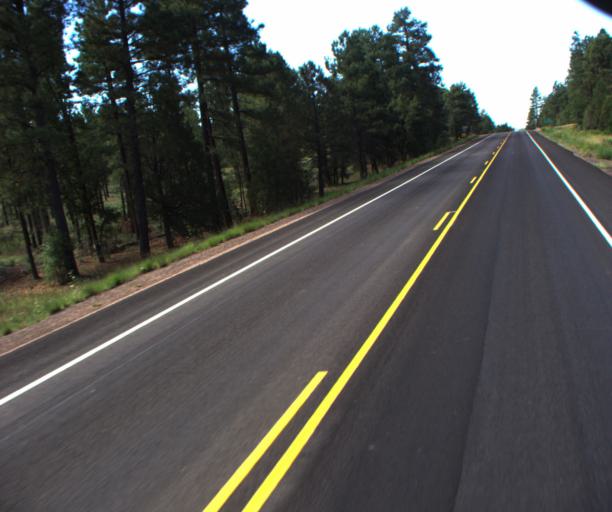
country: US
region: Arizona
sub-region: Navajo County
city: Show Low
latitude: 34.2058
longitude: -110.0799
